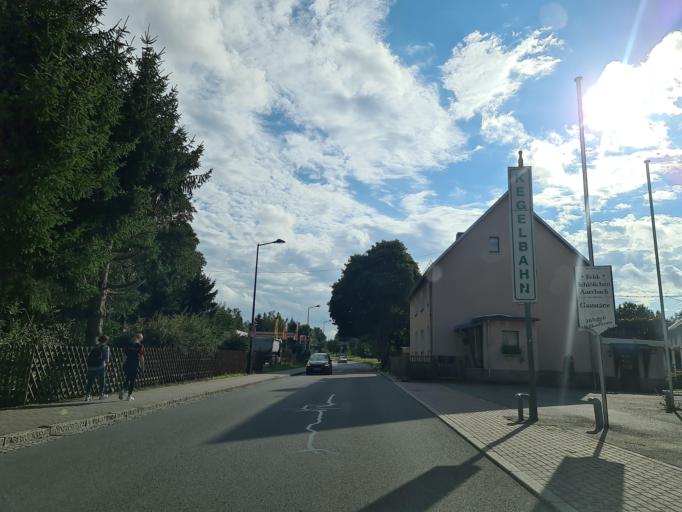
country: DE
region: Saxony
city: Auerbach
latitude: 50.5075
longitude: 12.3811
